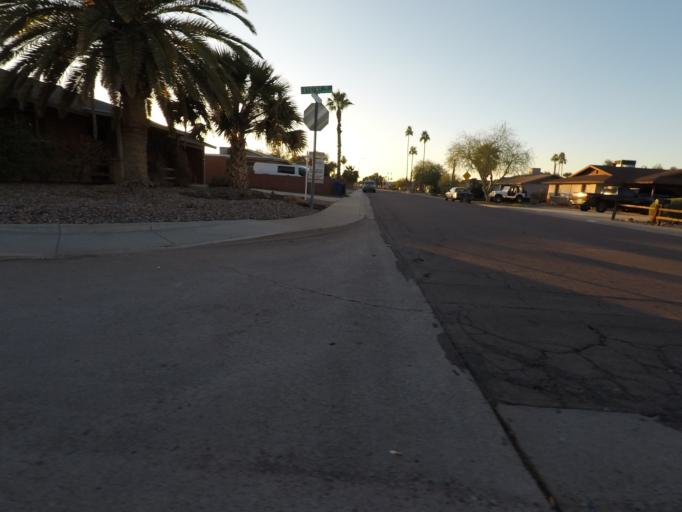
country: US
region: Arizona
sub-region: Maricopa County
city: Guadalupe
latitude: 33.3872
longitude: -111.9437
